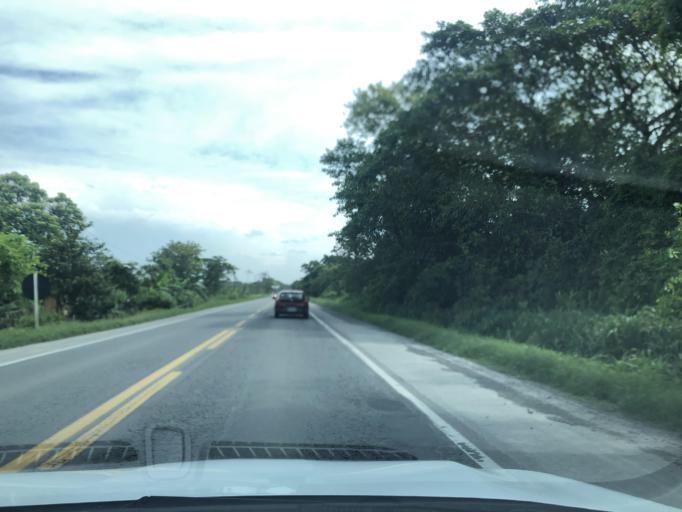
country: BR
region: Santa Catarina
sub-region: Sao Francisco Do Sul
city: Sao Francisco do Sul
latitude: -26.3486
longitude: -48.6584
